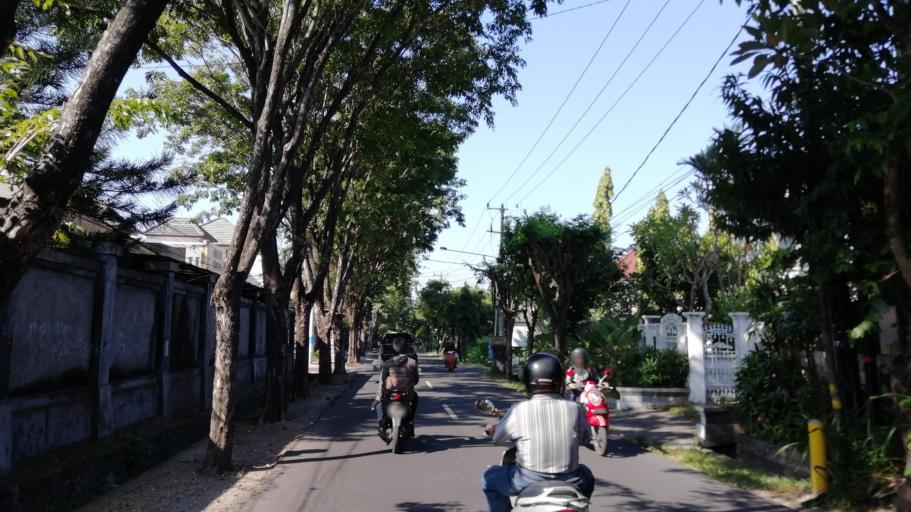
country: ID
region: Bali
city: Banjar Taman
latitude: -8.6744
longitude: 115.2384
